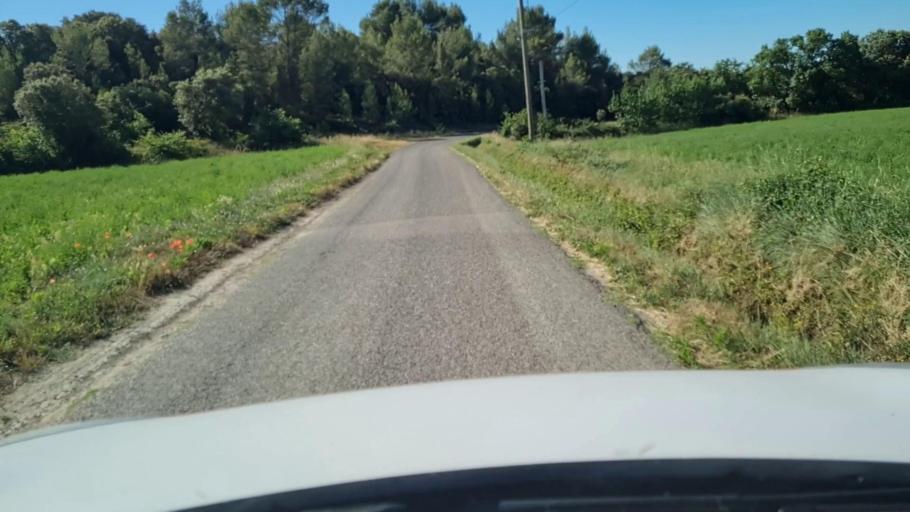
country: FR
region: Languedoc-Roussillon
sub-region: Departement du Gard
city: Sommieres
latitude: 43.8159
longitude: 4.0502
